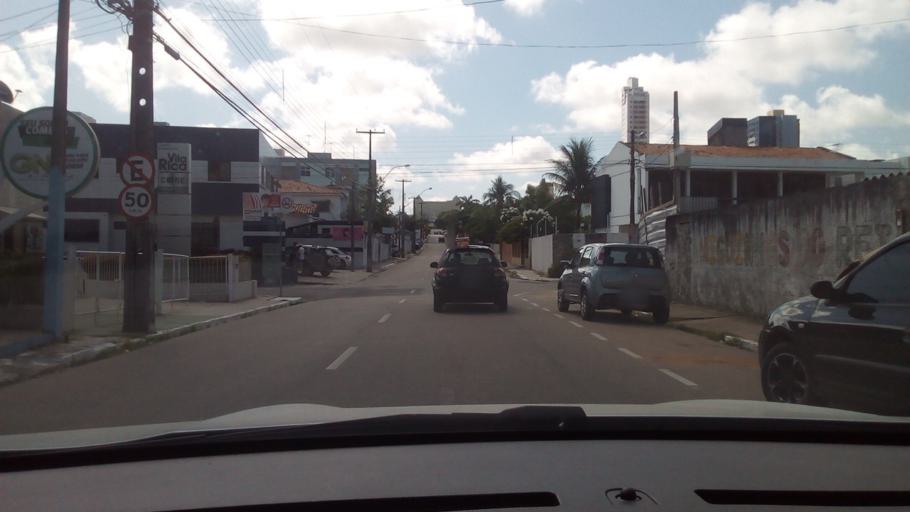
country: BR
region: Paraiba
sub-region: Joao Pessoa
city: Joao Pessoa
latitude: -7.1222
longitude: -34.8371
